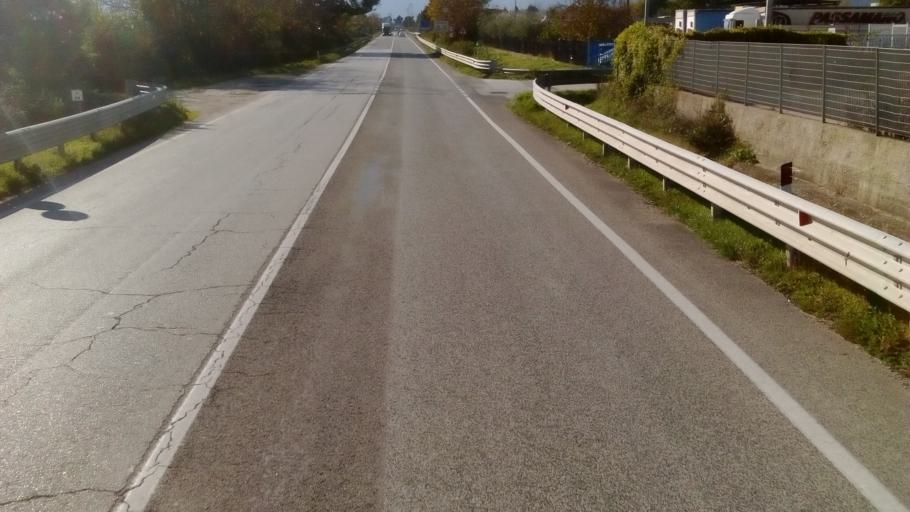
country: IT
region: Molise
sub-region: Provincia di Isernia
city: Taverna Ravindola
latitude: 41.5048
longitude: 14.1048
